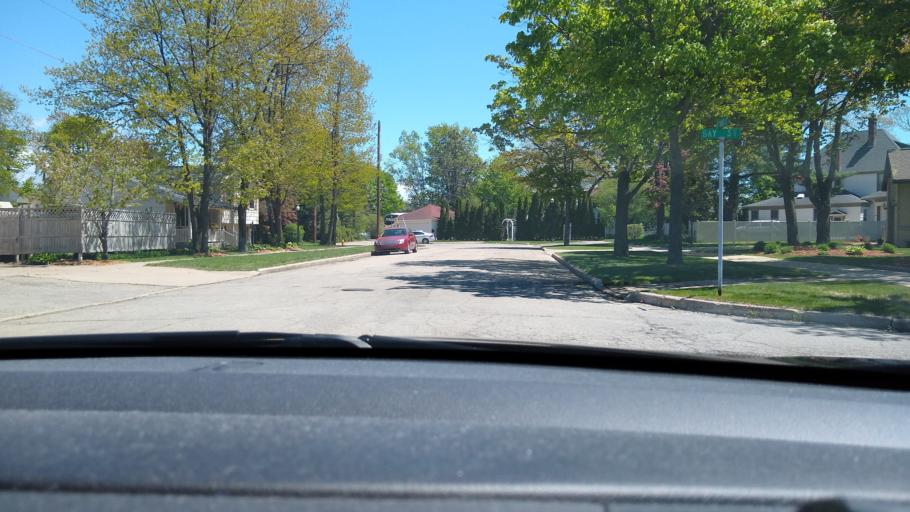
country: US
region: Michigan
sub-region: Delta County
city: Escanaba
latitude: 45.7383
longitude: -87.0591
